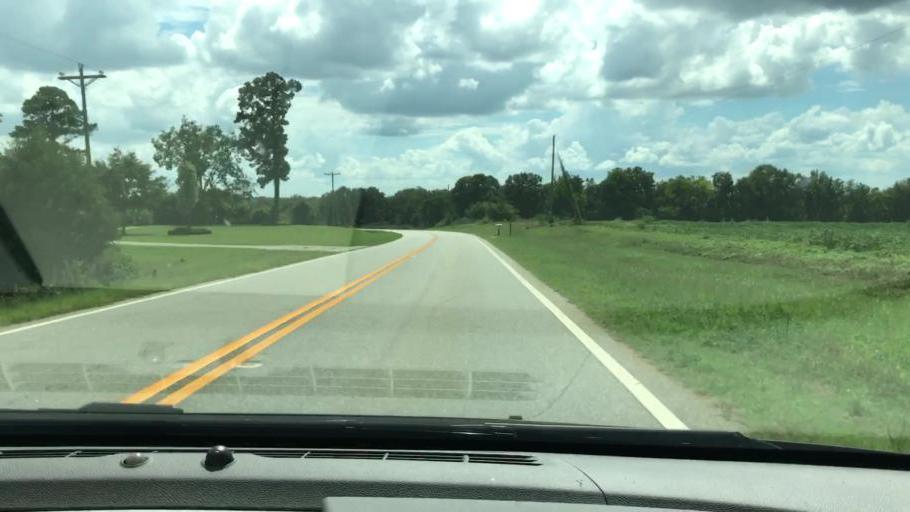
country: US
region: Georgia
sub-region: Quitman County
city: Georgetown
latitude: 31.9014
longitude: -85.0787
